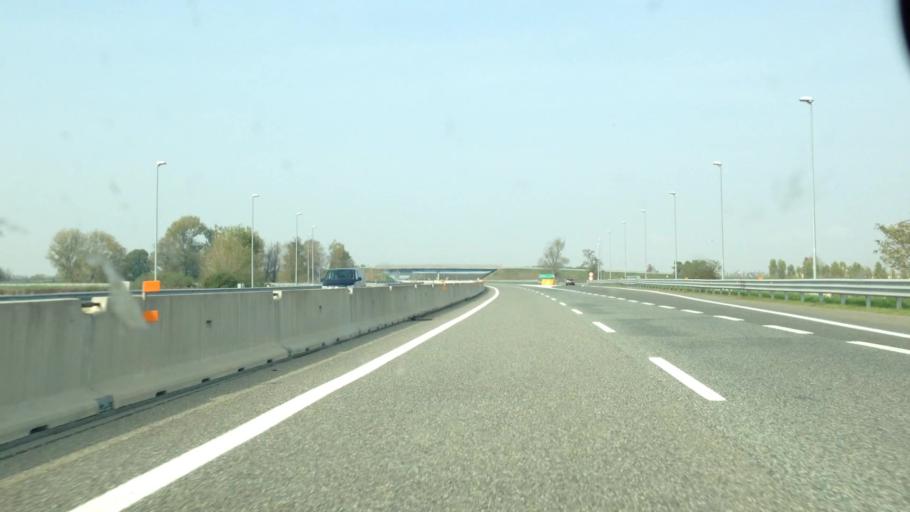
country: IT
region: Piedmont
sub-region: Provincia di Vercelli
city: Asigliano Vercellese
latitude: 45.2886
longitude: 8.3935
